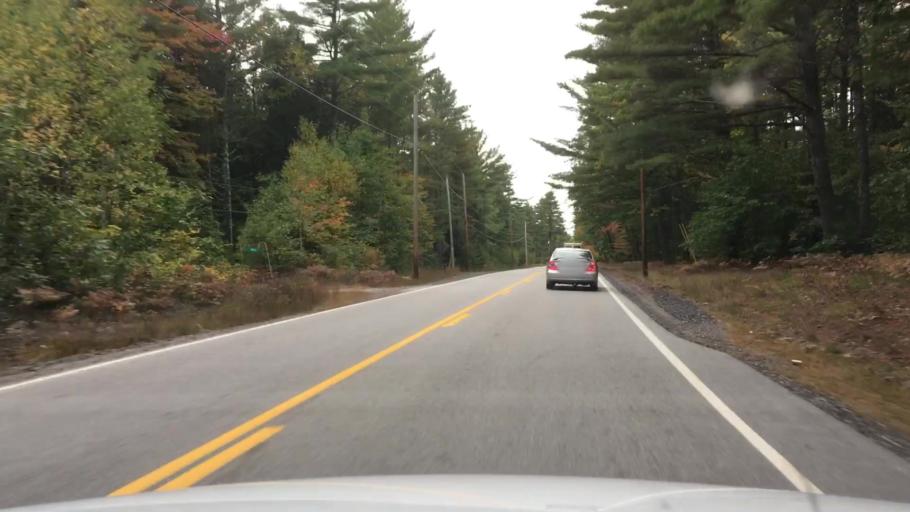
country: US
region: Maine
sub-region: Cumberland County
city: Harrison
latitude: 44.2135
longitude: -70.6819
